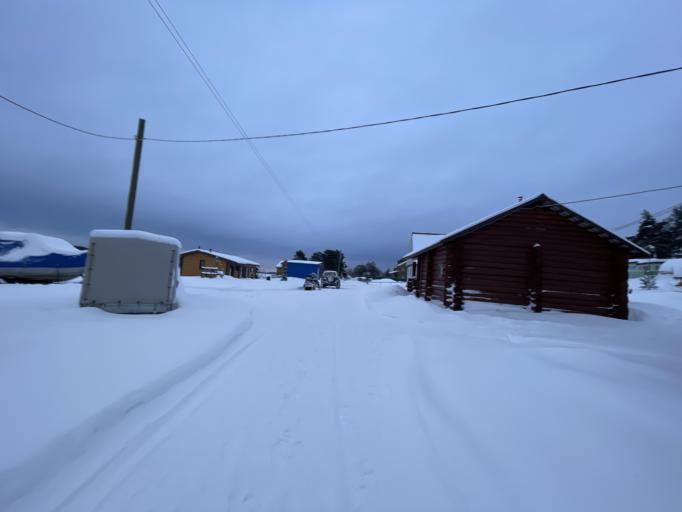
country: RU
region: Republic of Karelia
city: Kondopoga
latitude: 62.1743
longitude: 34.6354
